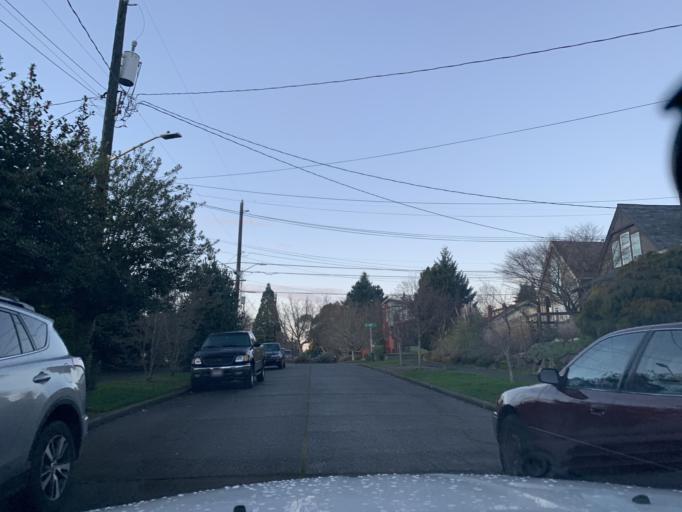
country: US
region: Washington
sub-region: King County
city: Shoreline
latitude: 47.6899
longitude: -122.3257
